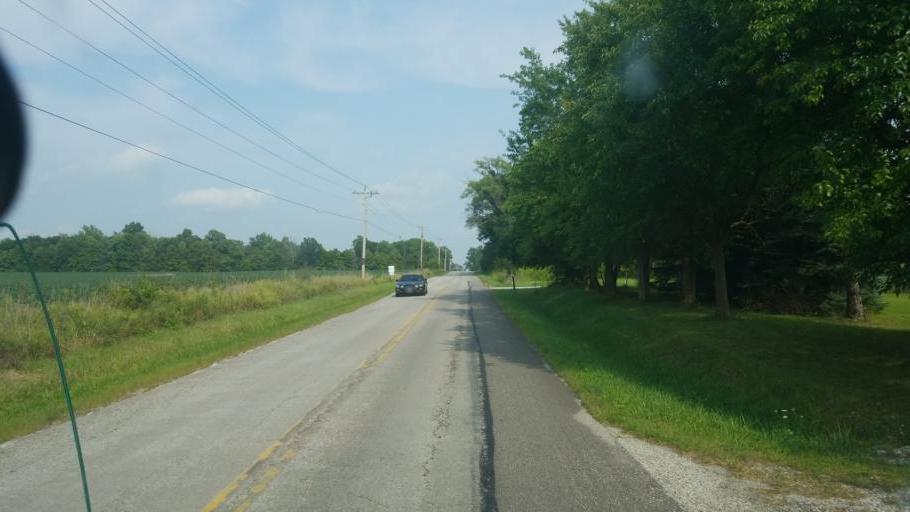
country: US
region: Ohio
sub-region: Medina County
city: Lodi
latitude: 41.1361
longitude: -82.0381
